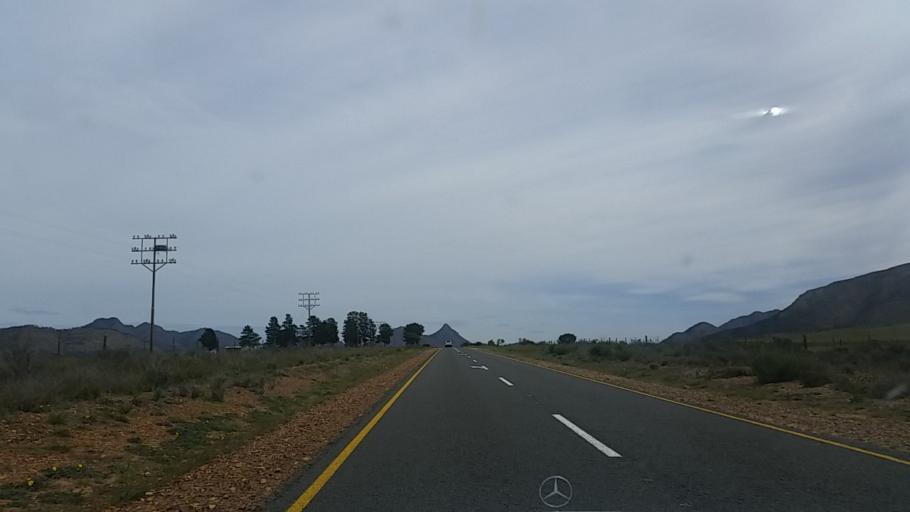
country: ZA
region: Western Cape
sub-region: Eden District Municipality
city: George
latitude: -33.8190
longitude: 22.5013
